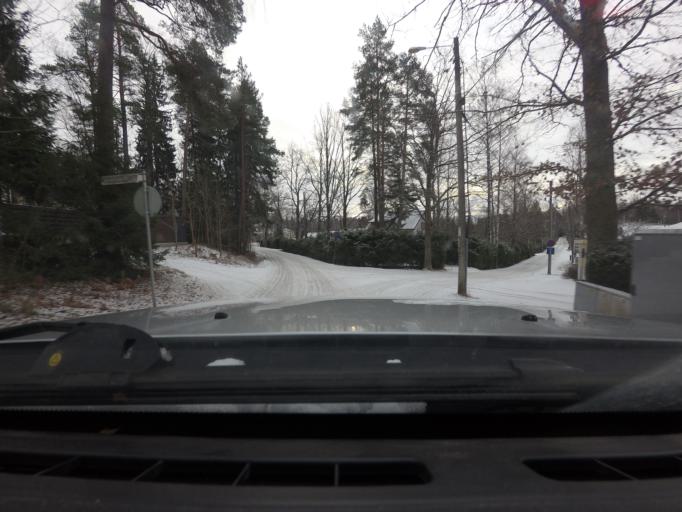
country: FI
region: Uusimaa
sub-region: Helsinki
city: Kilo
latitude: 60.2238
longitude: 24.7652
